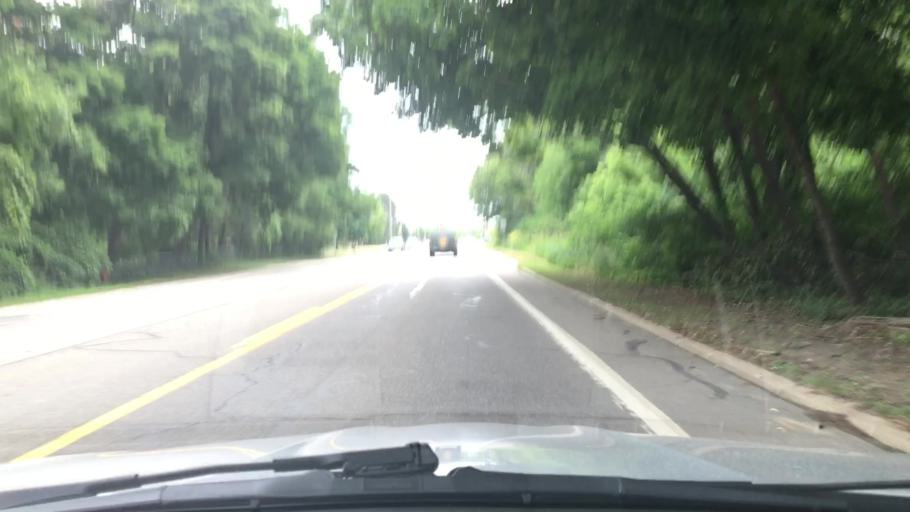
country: US
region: Michigan
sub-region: Wayne County
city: Northville
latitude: 42.4243
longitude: -83.4414
